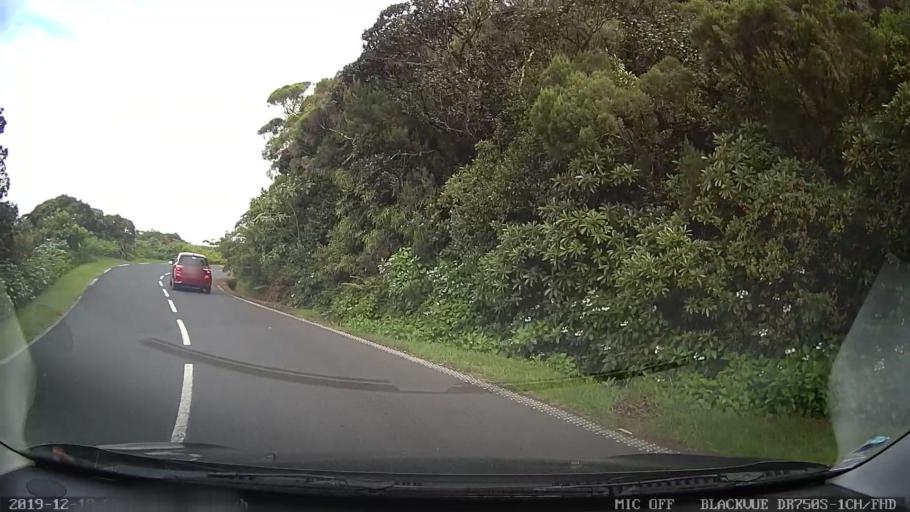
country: RE
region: Reunion
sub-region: Reunion
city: Cilaos
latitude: -21.1633
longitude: 55.5923
